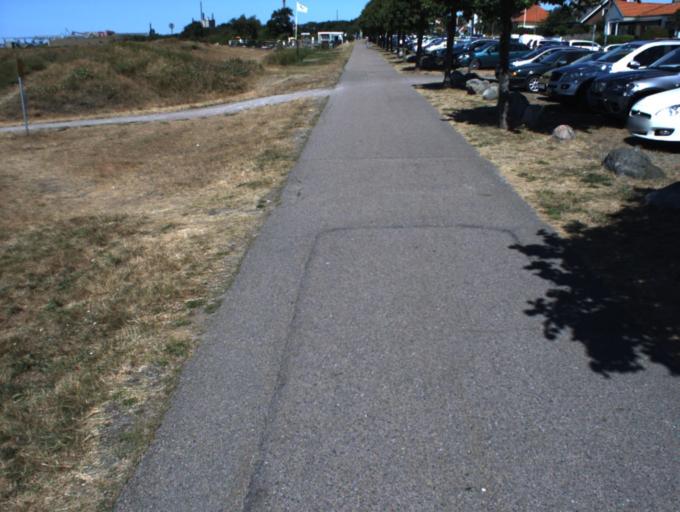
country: SE
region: Skane
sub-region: Helsingborg
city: Rydeback
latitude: 56.0006
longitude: 12.7340
